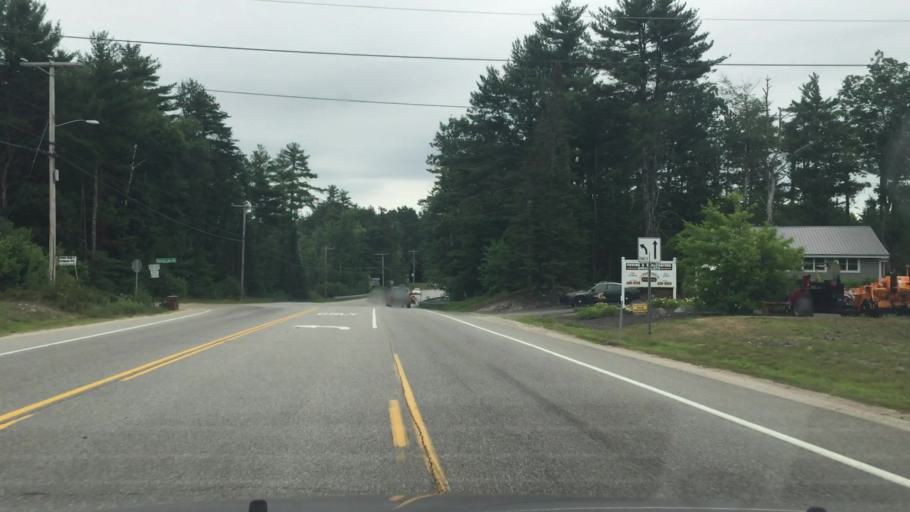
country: US
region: New Hampshire
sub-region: Carroll County
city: Ossipee
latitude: 43.7011
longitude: -71.1079
